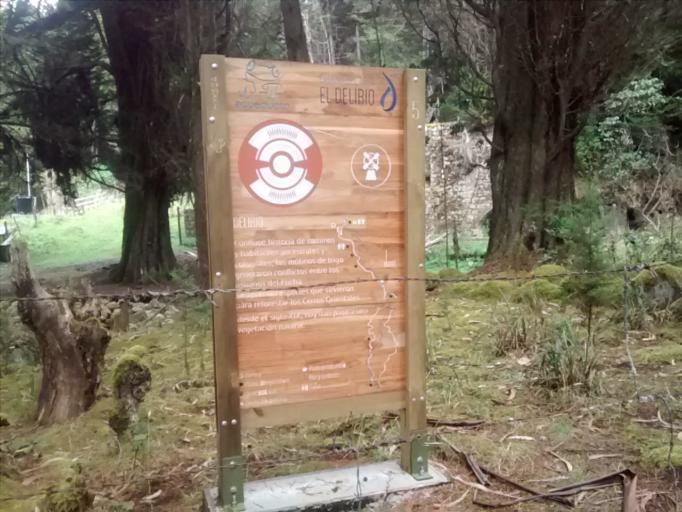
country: CO
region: Bogota D.C.
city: Bogota
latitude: 4.5529
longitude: -74.0582
